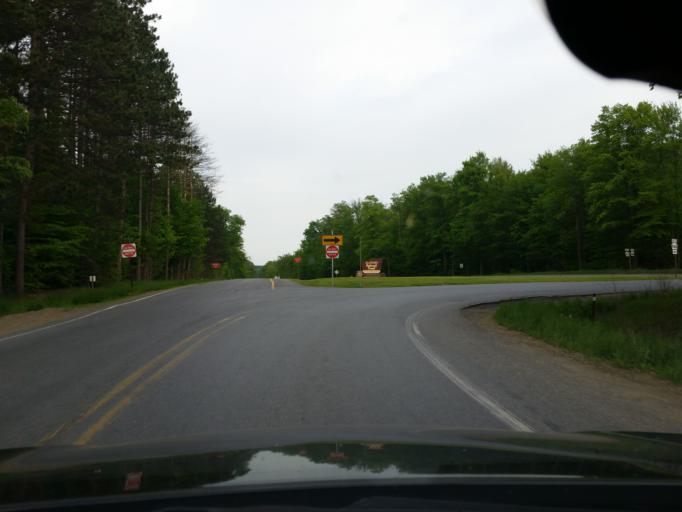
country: US
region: Pennsylvania
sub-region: McKean County
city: Kane
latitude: 41.5807
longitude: -78.9339
